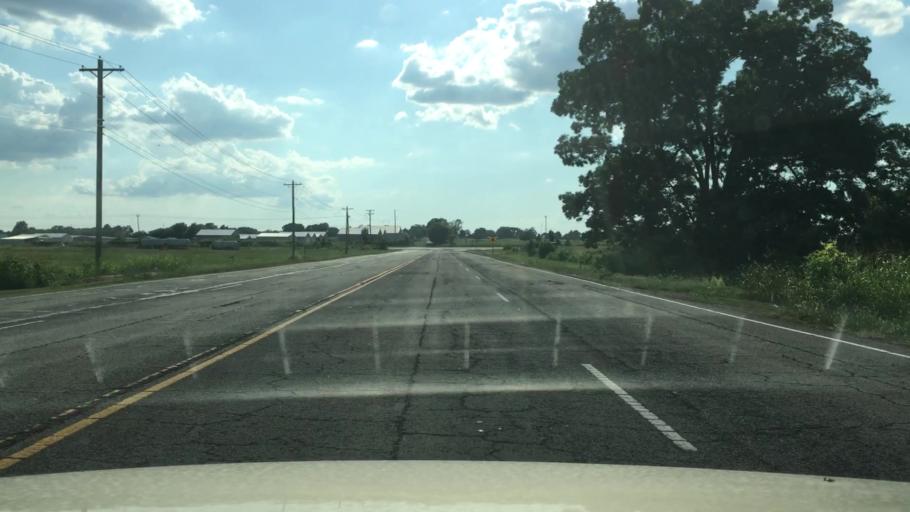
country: US
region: Oklahoma
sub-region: Cherokee County
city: Tahlequah
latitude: 35.9299
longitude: -94.9973
